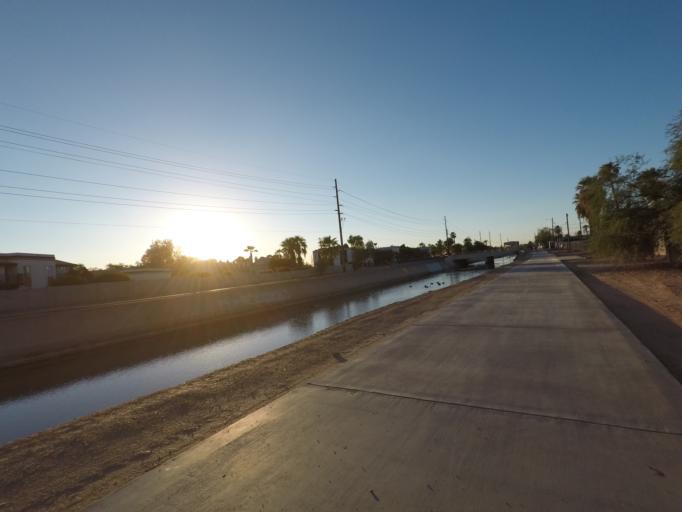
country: US
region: Arizona
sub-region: Maricopa County
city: Phoenix
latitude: 33.4983
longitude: -112.0533
